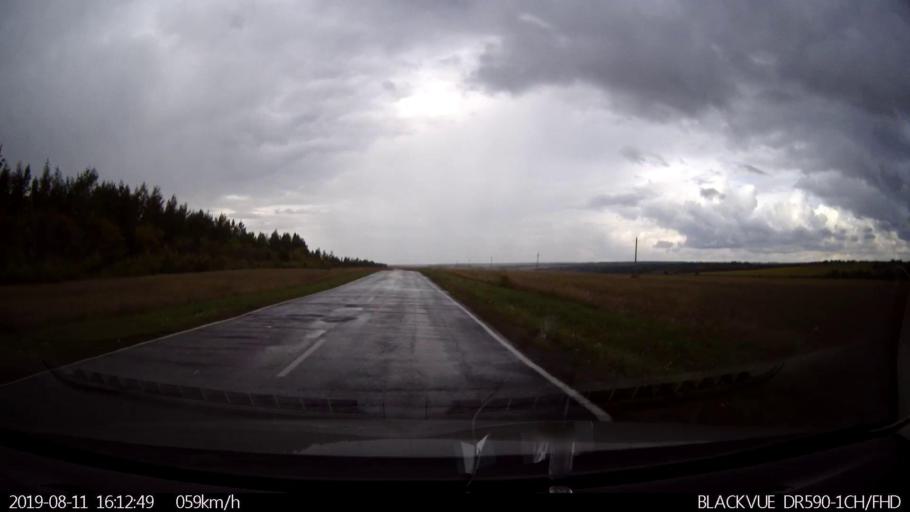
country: RU
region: Ulyanovsk
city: Ignatovka
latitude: 54.0147
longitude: 47.6392
